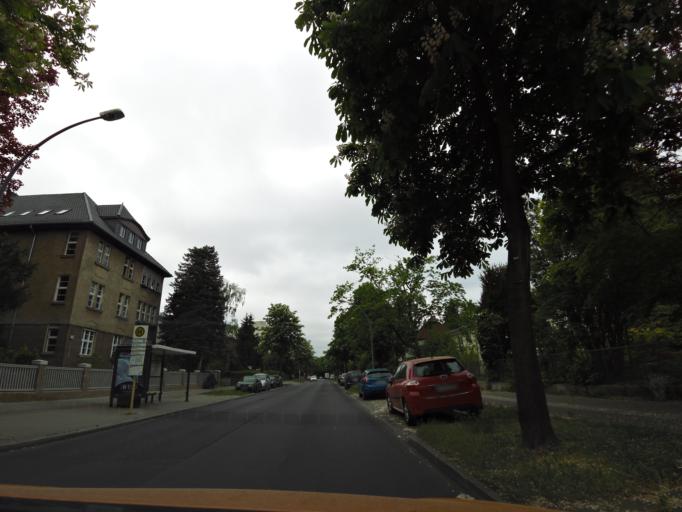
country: DE
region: Berlin
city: Zehlendorf Bezirk
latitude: 52.4211
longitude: 13.2500
